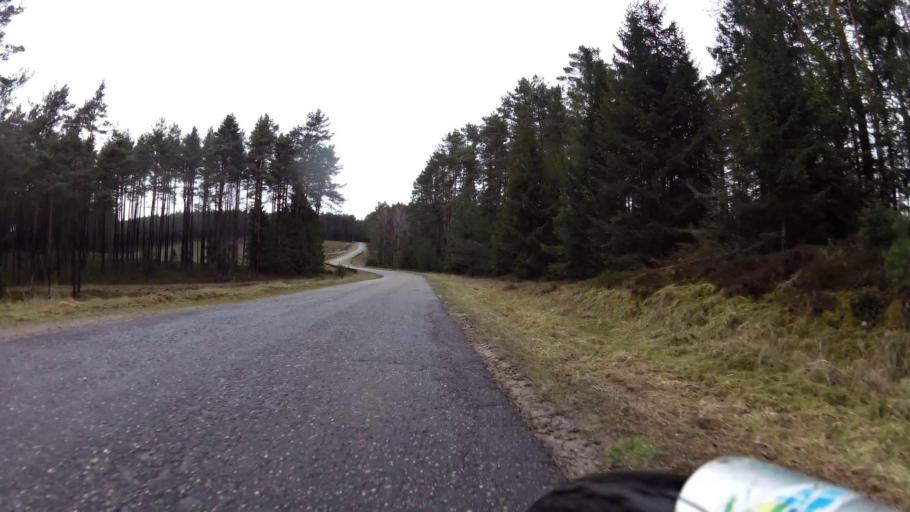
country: PL
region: Pomeranian Voivodeship
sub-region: Powiat bytowski
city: Borzytuchom
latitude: 54.2654
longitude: 17.3665
